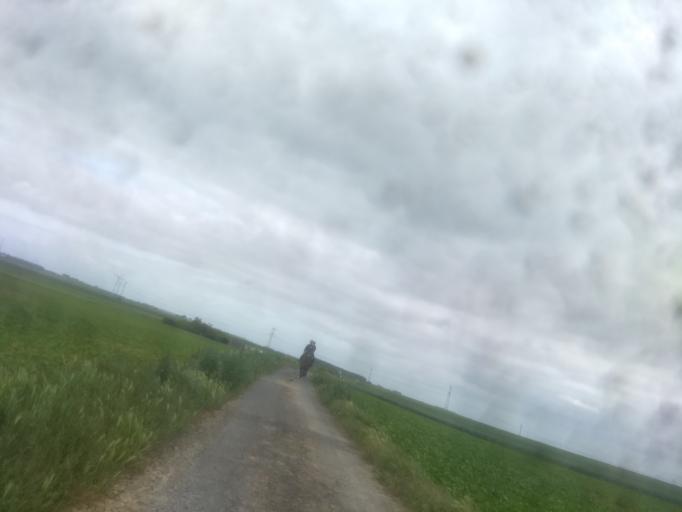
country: FR
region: Nord-Pas-de-Calais
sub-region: Departement du Pas-de-Calais
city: Tilloy-les-Mofflaines
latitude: 50.2692
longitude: 2.8139
